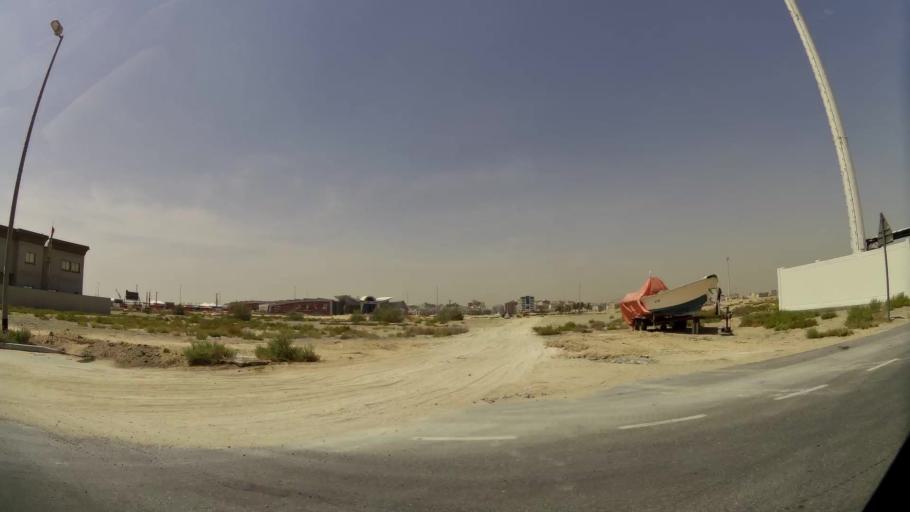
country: AE
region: Ash Shariqah
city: Sharjah
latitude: 25.1794
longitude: 55.4128
